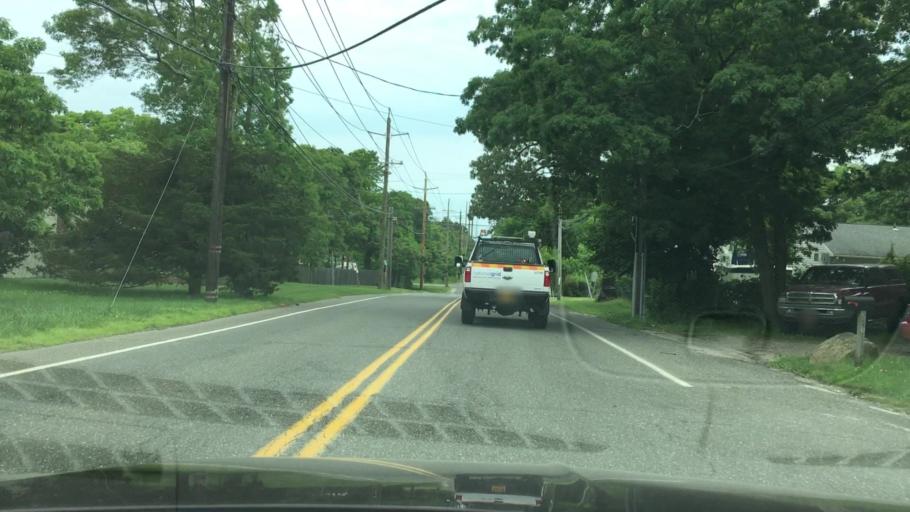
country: US
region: New York
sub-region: Suffolk County
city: Holbrook
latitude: 40.8125
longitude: -73.0755
